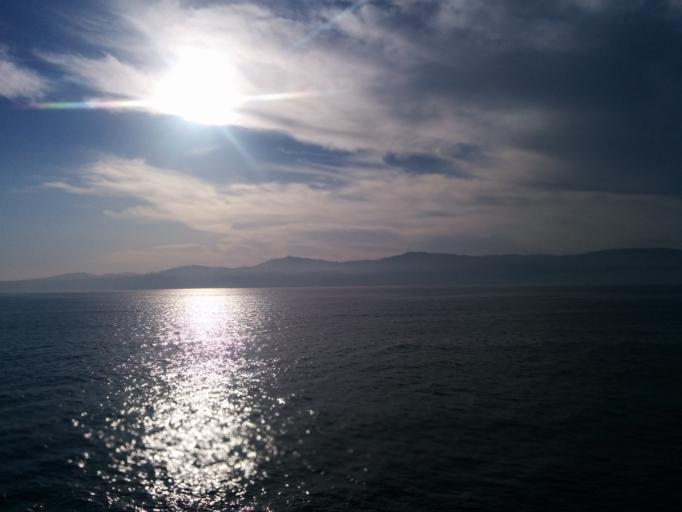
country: MA
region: Tanger-Tetouan
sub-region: Tanger-Assilah
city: Tangier
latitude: 35.8179
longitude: -5.7782
